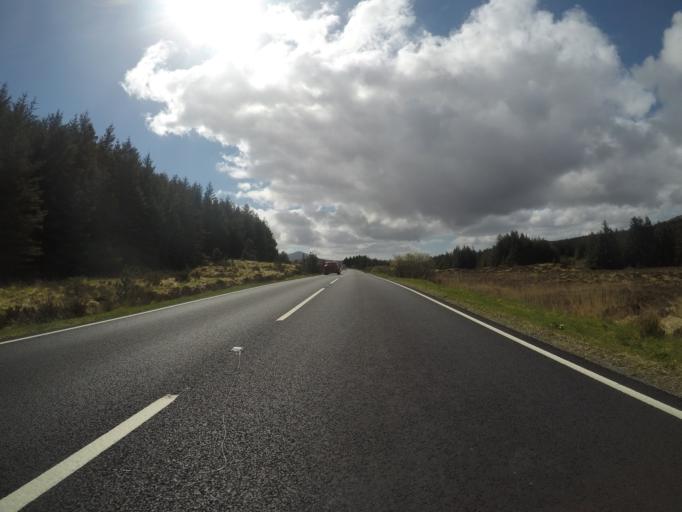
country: GB
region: Scotland
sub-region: Highland
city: Isle of Skye
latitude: 57.3305
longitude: -6.2019
